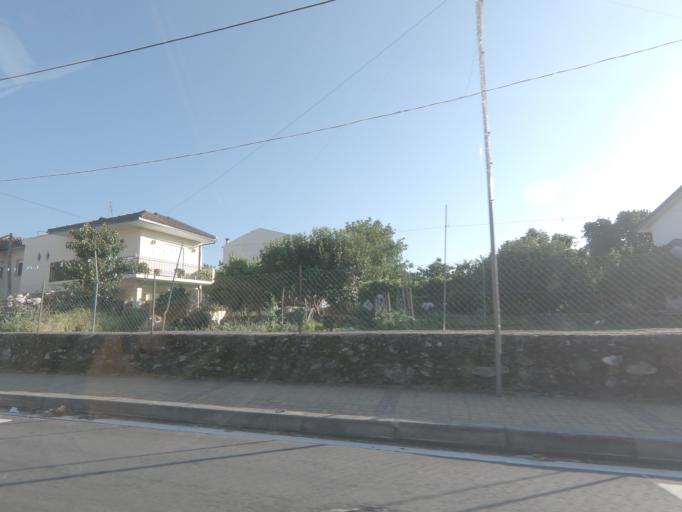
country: PT
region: Vila Real
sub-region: Vila Real
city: Vila Real
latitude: 41.2830
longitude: -7.6978
